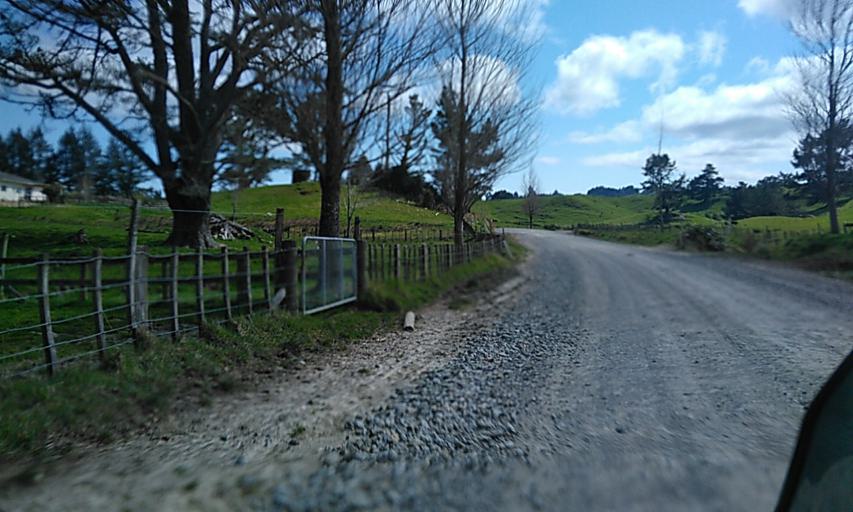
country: NZ
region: Gisborne
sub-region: Gisborne District
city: Gisborne
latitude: -38.2165
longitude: 178.0729
